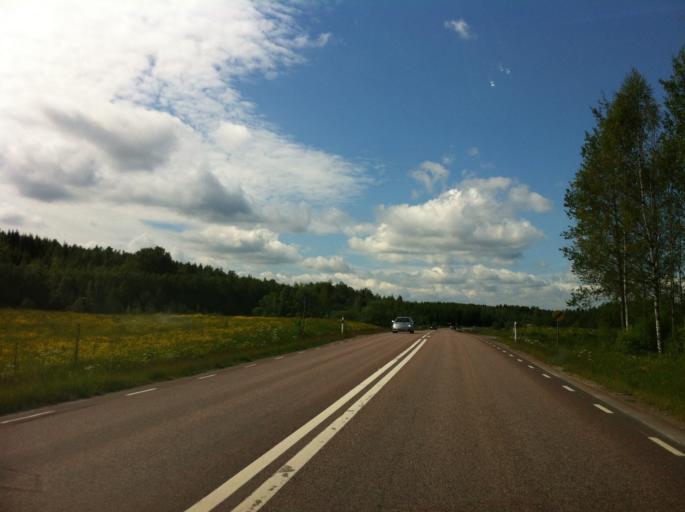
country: SE
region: Vaermland
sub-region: Karlstads Kommun
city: Valberg
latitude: 59.3759
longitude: 13.1539
